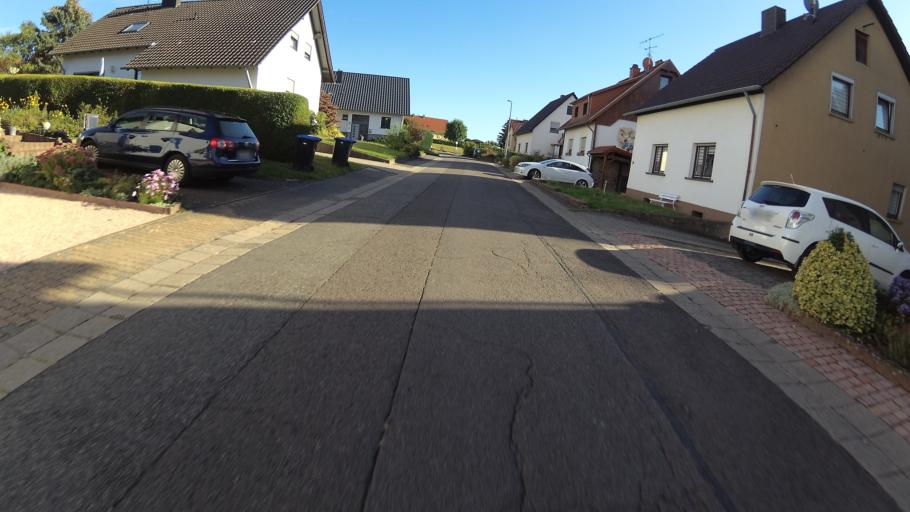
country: DE
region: Saarland
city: Eppelborn
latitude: 49.3565
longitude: 6.9969
